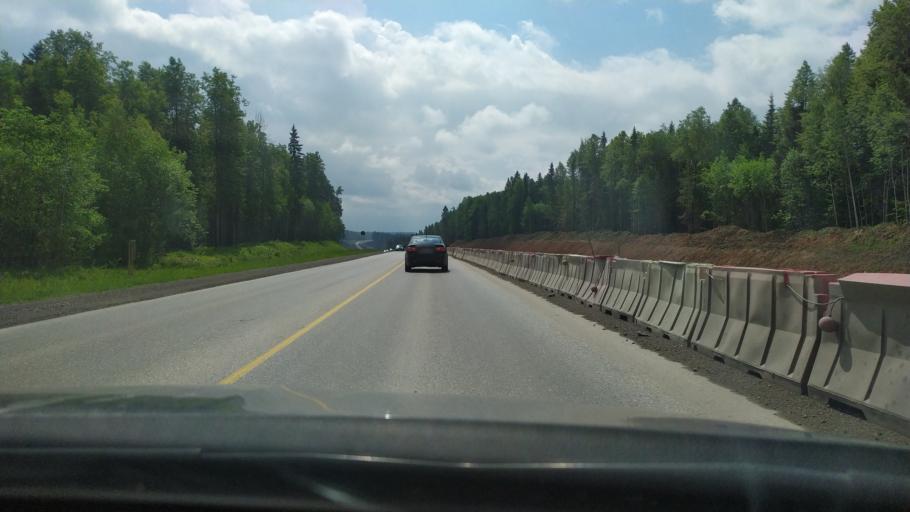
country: RU
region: Perm
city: Novyye Lyady
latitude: 58.0995
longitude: 56.4250
